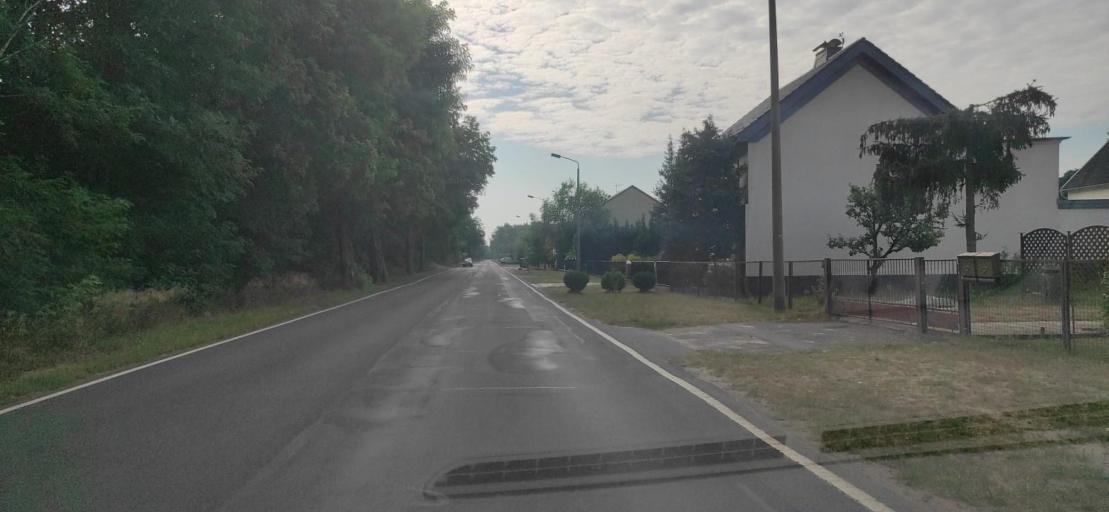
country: DE
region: Brandenburg
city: Forst
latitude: 51.7163
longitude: 14.6648
